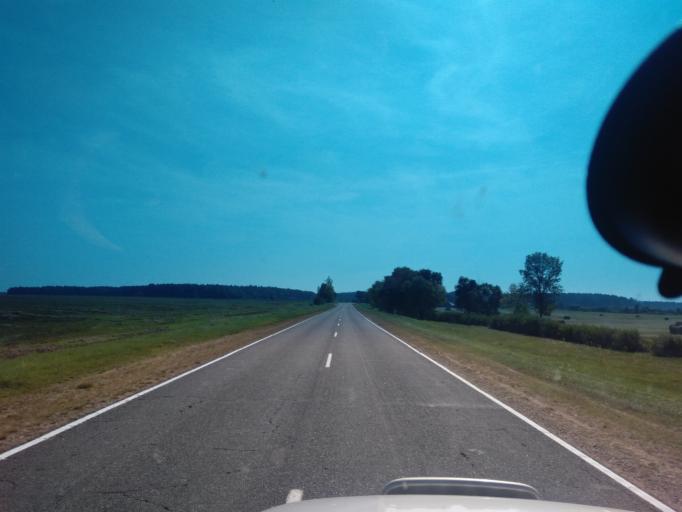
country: BY
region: Minsk
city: Uzda
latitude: 53.3931
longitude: 27.2369
